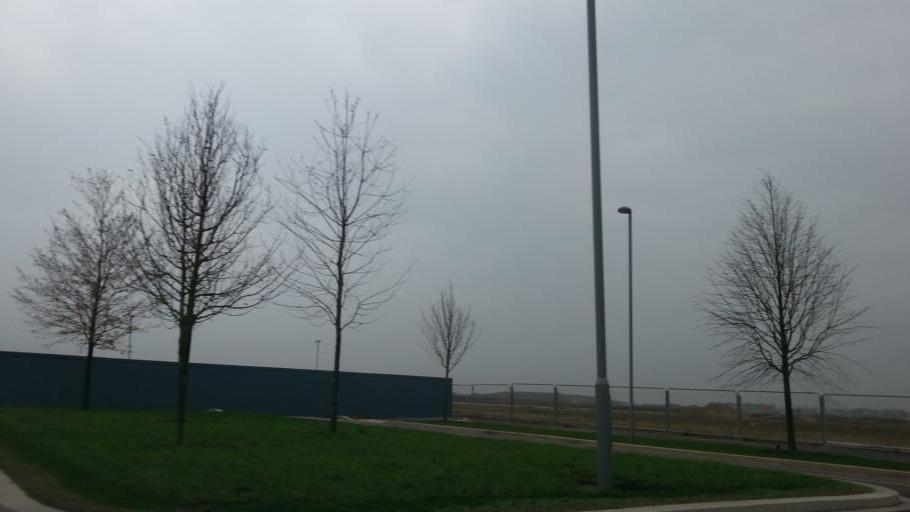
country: GB
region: England
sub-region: Cambridgeshire
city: Great Stukeley
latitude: 52.3764
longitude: -0.2358
